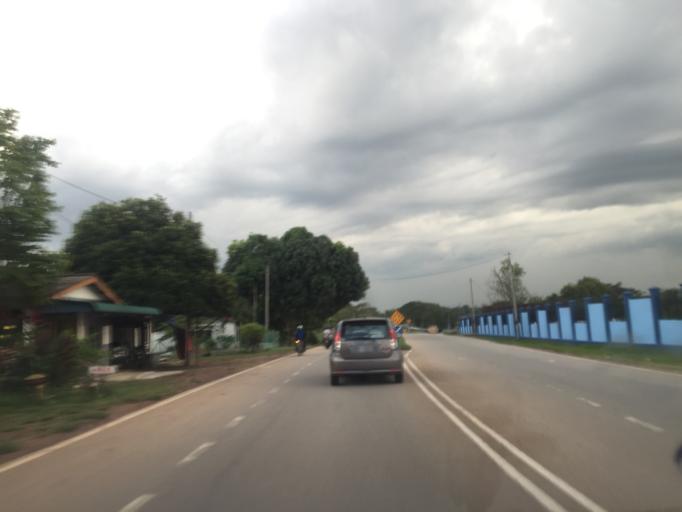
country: MY
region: Kedah
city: Sungai Petani
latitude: 5.5702
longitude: 100.5038
